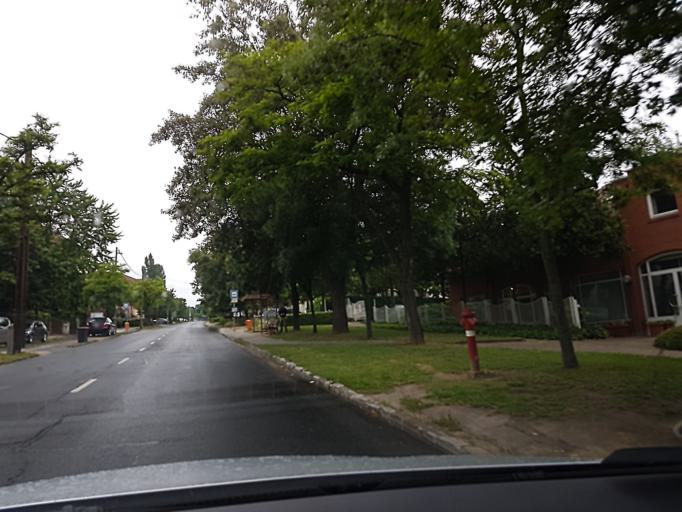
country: HU
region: Budapest
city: Budapest II. keruelet
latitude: 47.5240
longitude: 19.0138
